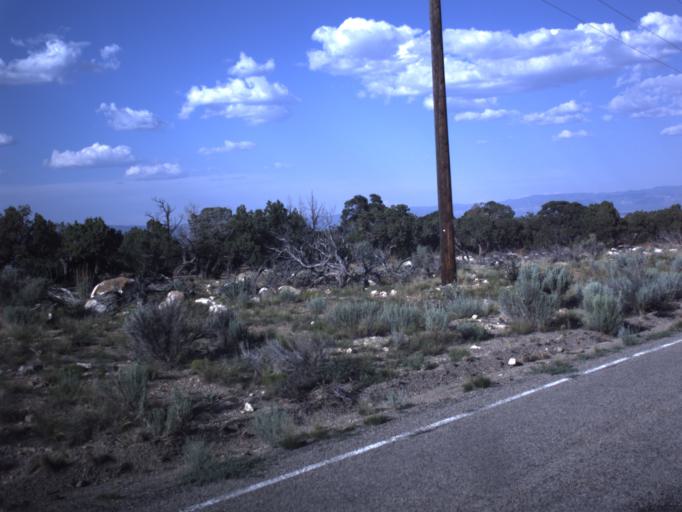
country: US
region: Utah
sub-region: Emery County
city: Huntington
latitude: 39.4869
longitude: -110.9444
